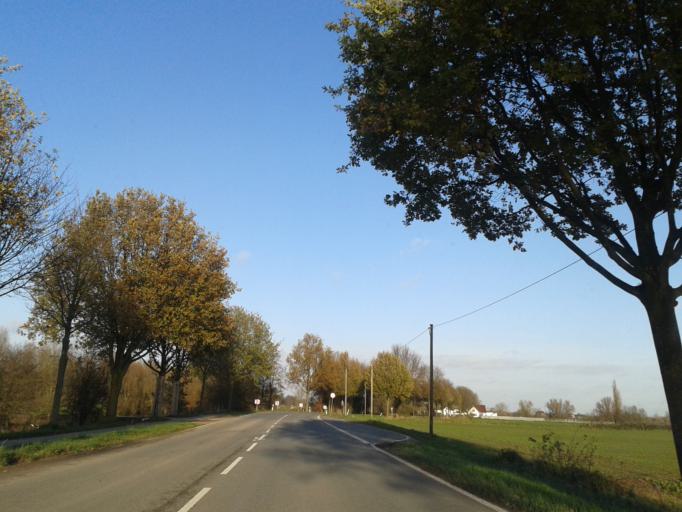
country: DE
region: North Rhine-Westphalia
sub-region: Regierungsbezirk Dusseldorf
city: Xanten
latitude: 51.6616
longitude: 6.4762
